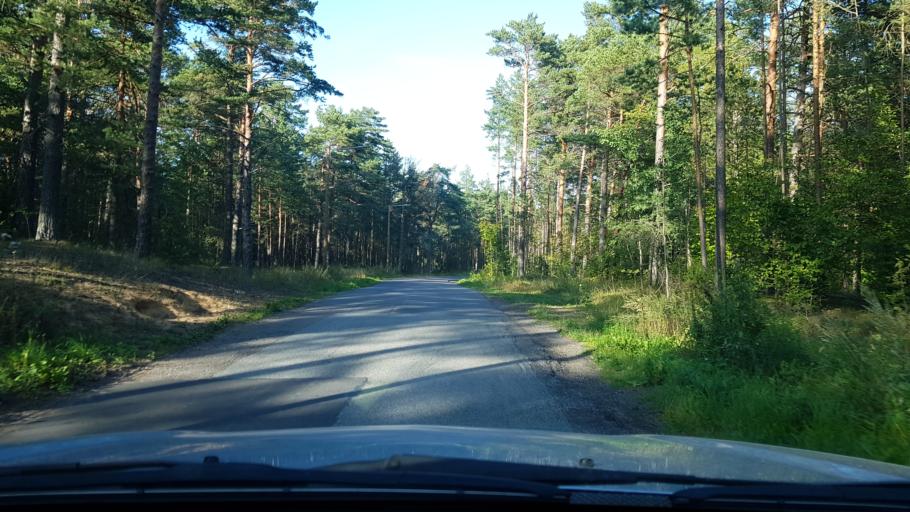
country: EE
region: Ida-Virumaa
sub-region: Narva-Joesuu linn
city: Narva-Joesuu
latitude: 59.4497
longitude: 28.0692
